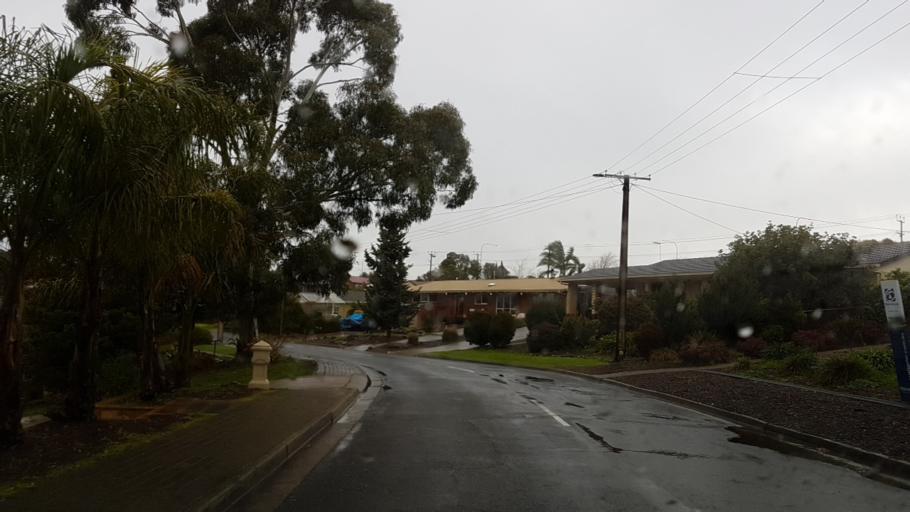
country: AU
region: South Australia
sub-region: Onkaparinga
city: Bedford Park
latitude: -35.0478
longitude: 138.5733
